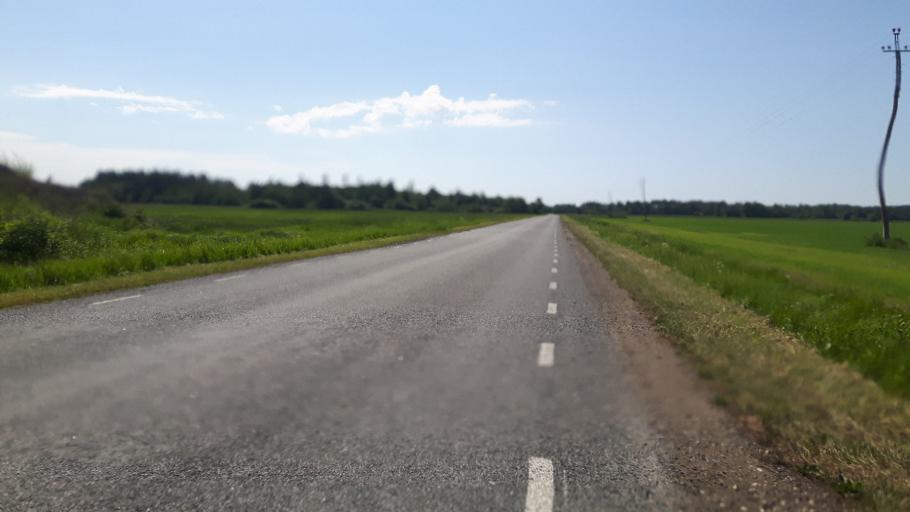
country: EE
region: Paernumaa
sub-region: Vaendra vald (alev)
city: Vandra
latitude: 58.6100
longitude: 25.0213
